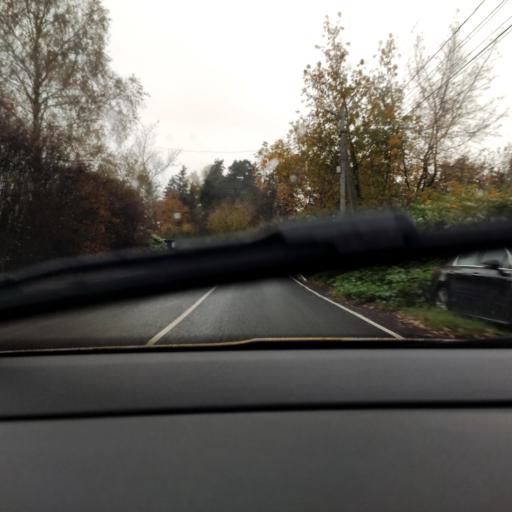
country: RU
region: Moskovskaya
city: Lesnyye Polyany
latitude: 55.9725
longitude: 37.8441
